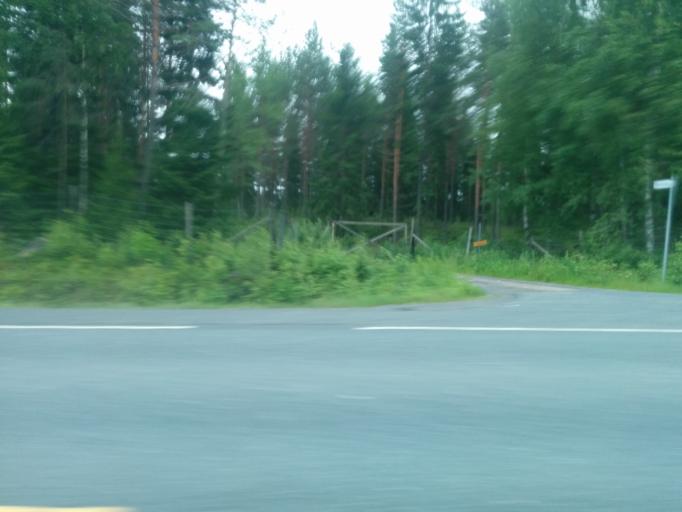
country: FI
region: Pirkanmaa
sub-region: Tampere
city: Orivesi
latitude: 61.6727
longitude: 24.2965
